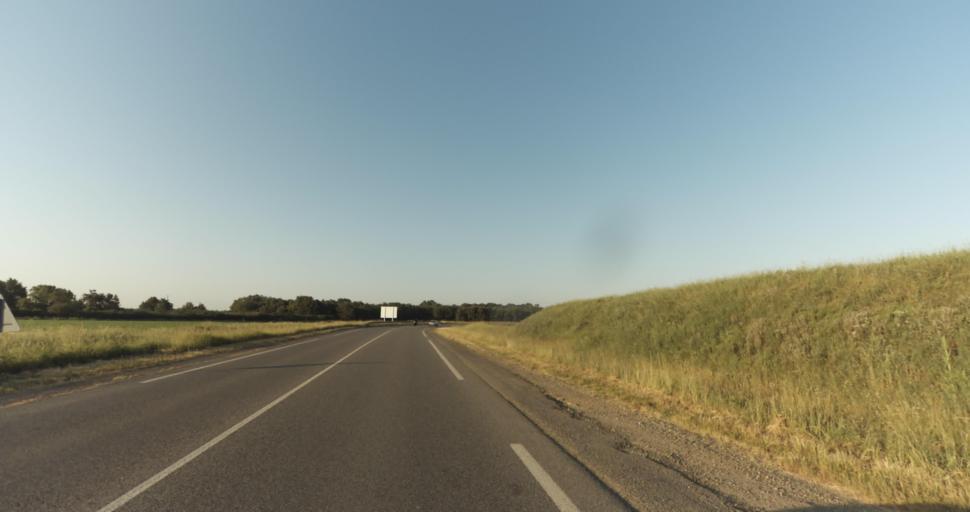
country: FR
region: Midi-Pyrenees
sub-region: Departement de la Haute-Garonne
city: Leguevin
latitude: 43.5796
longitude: 1.2175
